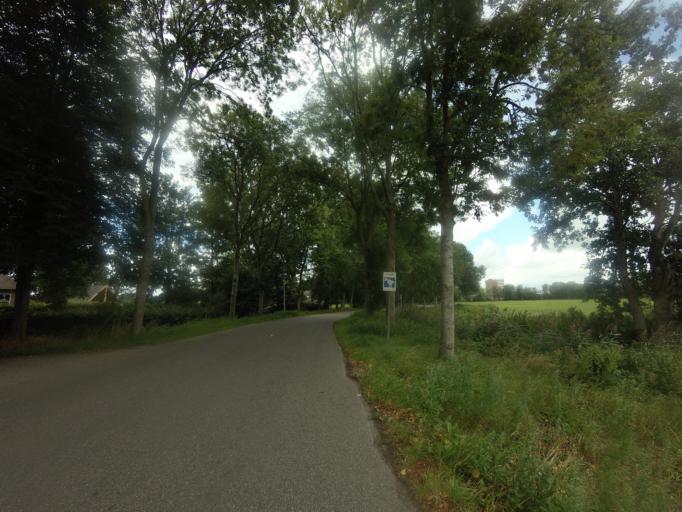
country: NL
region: Drenthe
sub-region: Gemeente Meppel
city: Meppel
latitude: 52.6865
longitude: 6.2148
